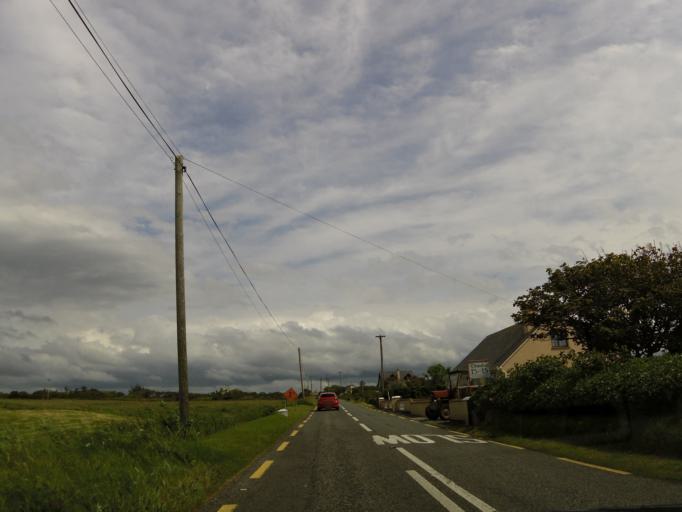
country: IE
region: Munster
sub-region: An Clar
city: Kilrush
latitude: 52.7621
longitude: -9.4719
